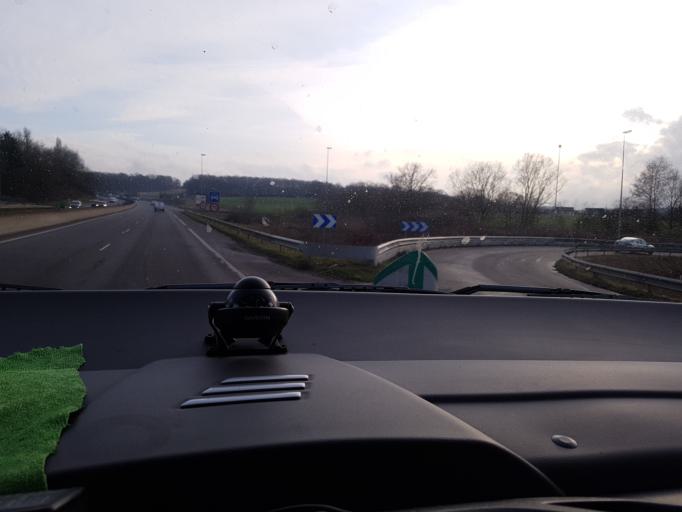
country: FR
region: Champagne-Ardenne
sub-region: Departement des Ardennes
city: Prix-les-Mezieres
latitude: 49.7532
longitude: 4.7025
